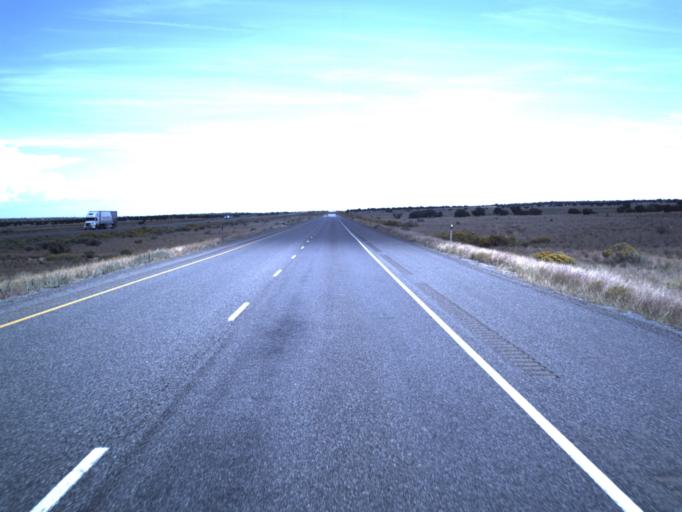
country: US
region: Utah
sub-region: Emery County
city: Castle Dale
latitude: 38.8923
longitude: -110.6306
